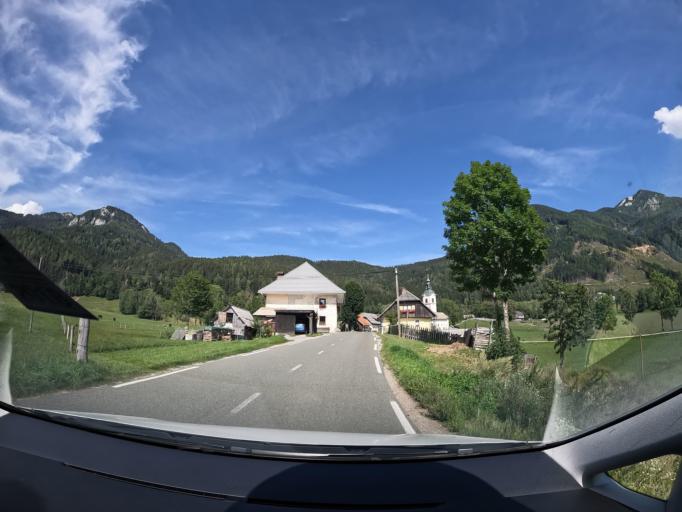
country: AT
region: Carinthia
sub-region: Politischer Bezirk Feldkirchen
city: Feldkirchen in Karnten
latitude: 46.7360
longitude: 14.1492
